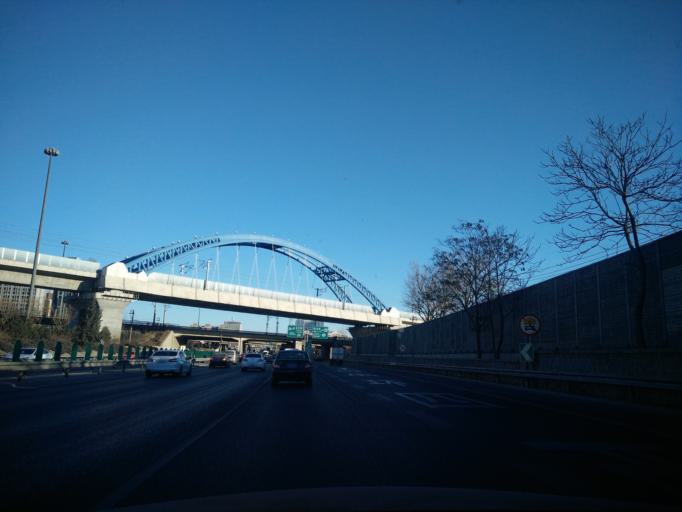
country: CN
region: Beijing
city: Lugu
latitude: 39.8895
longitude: 116.2054
